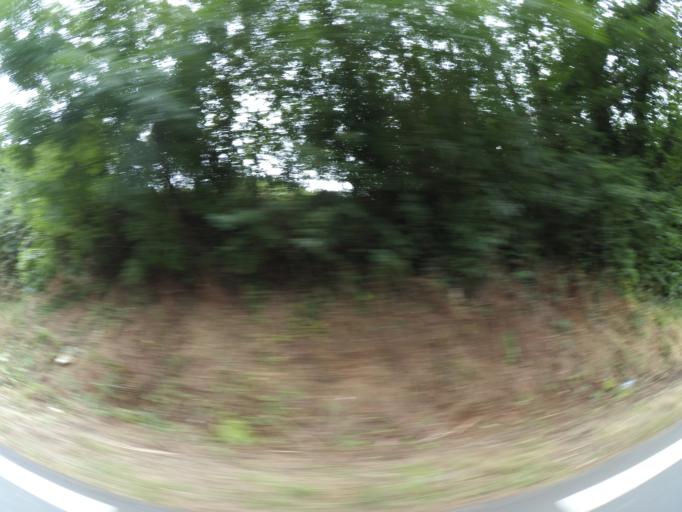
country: FR
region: Brittany
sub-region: Departement des Cotes-d'Armor
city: Tremuson
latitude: 48.5231
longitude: -2.8189
